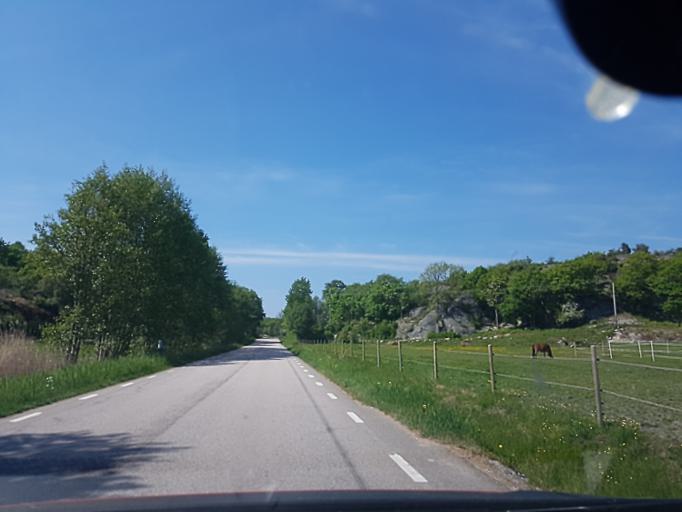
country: SE
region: Vaestra Goetaland
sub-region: Lysekils Kommun
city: Lysekil
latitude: 58.1623
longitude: 11.4533
